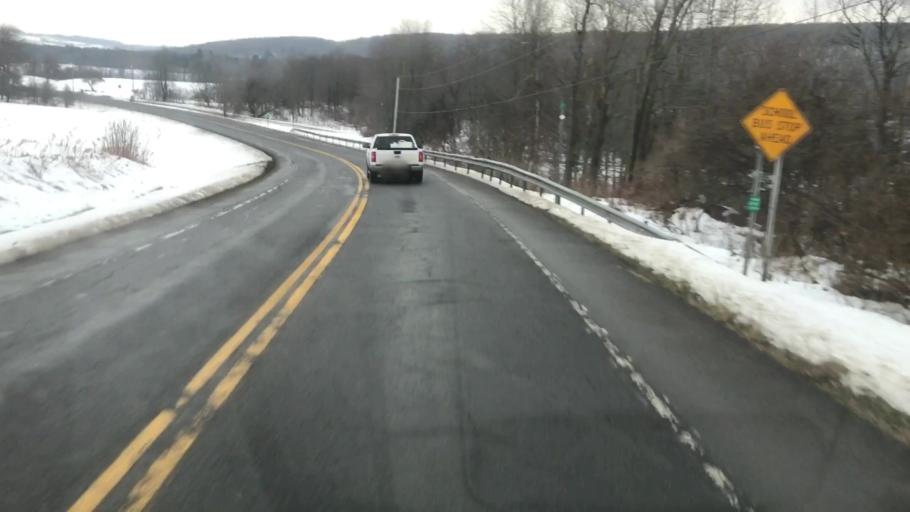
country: US
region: New York
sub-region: Tompkins County
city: Groton
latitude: 42.6834
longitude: -76.3012
